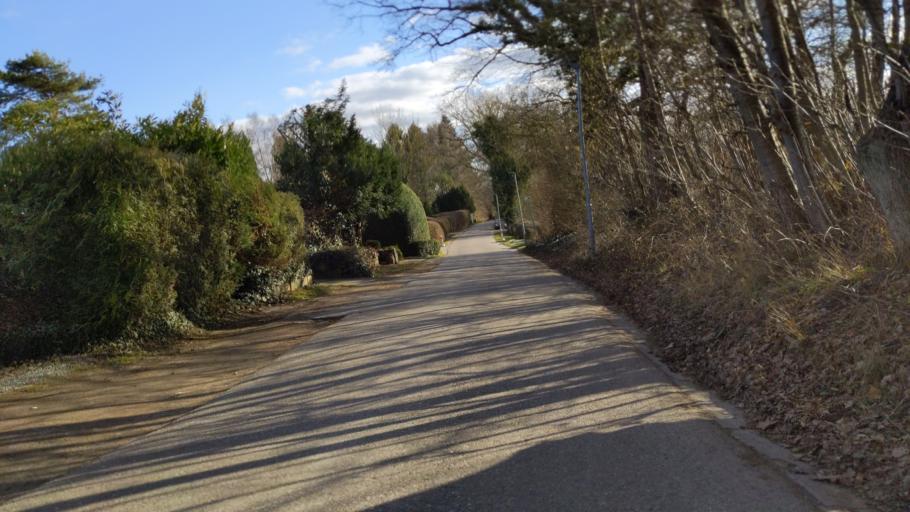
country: DE
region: Schleswig-Holstein
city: Timmendorfer Strand
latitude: 53.9990
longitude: 10.7561
